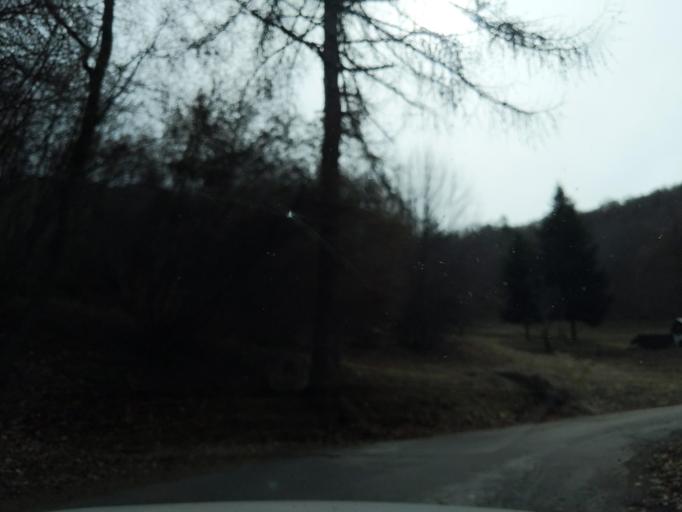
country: FR
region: Rhone-Alpes
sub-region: Departement de la Savoie
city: Villargondran
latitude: 45.2572
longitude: 6.3662
